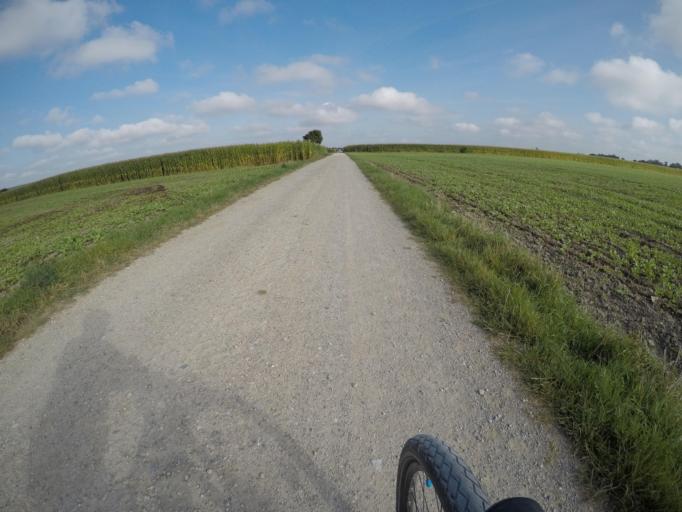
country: DE
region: Bavaria
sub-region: Swabia
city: Meitingen
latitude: 48.5632
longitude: 10.8515
